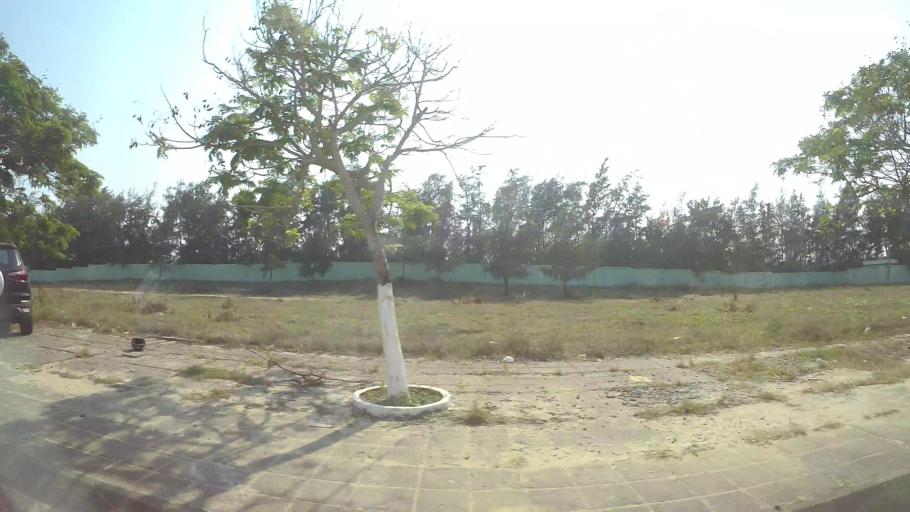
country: VN
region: Da Nang
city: Ngu Hanh Son
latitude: 15.9629
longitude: 108.2877
